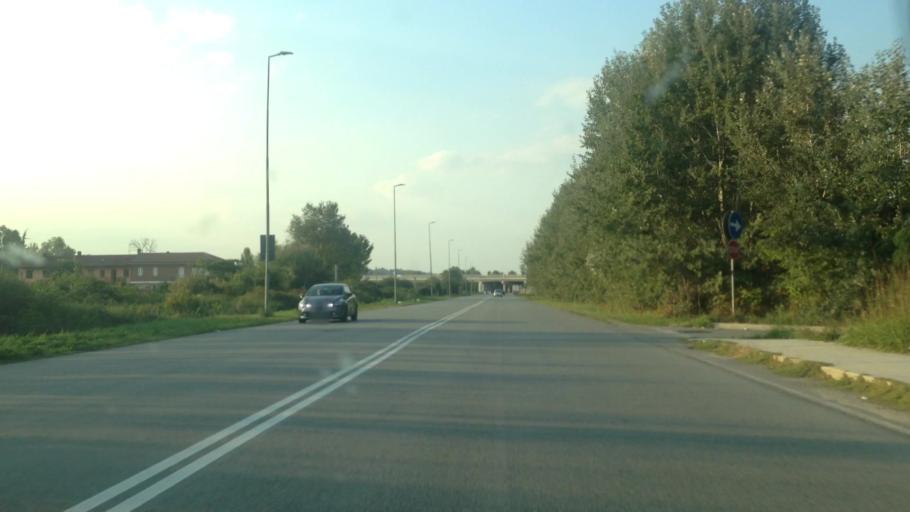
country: IT
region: Piedmont
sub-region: Provincia di Asti
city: Asti
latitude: 44.9083
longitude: 8.2308
